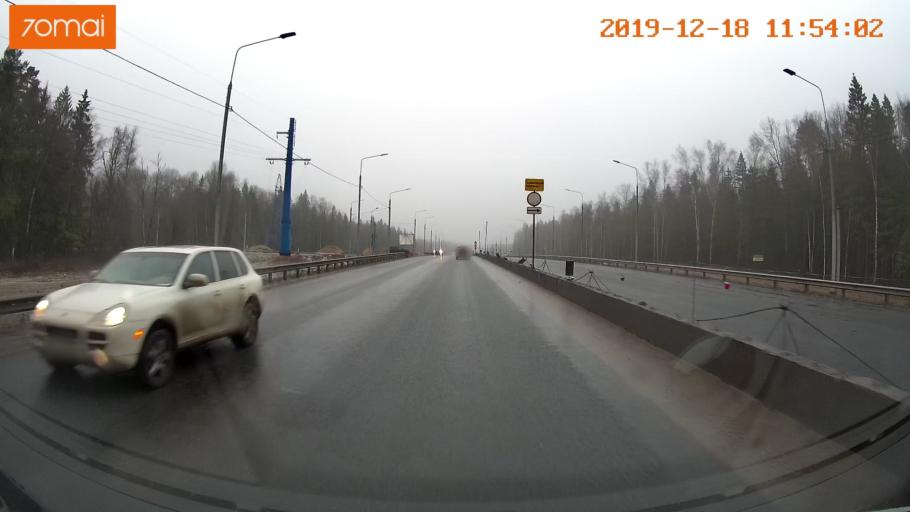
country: RU
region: Moskovskaya
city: Yershovo
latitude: 55.8113
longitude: 36.9188
